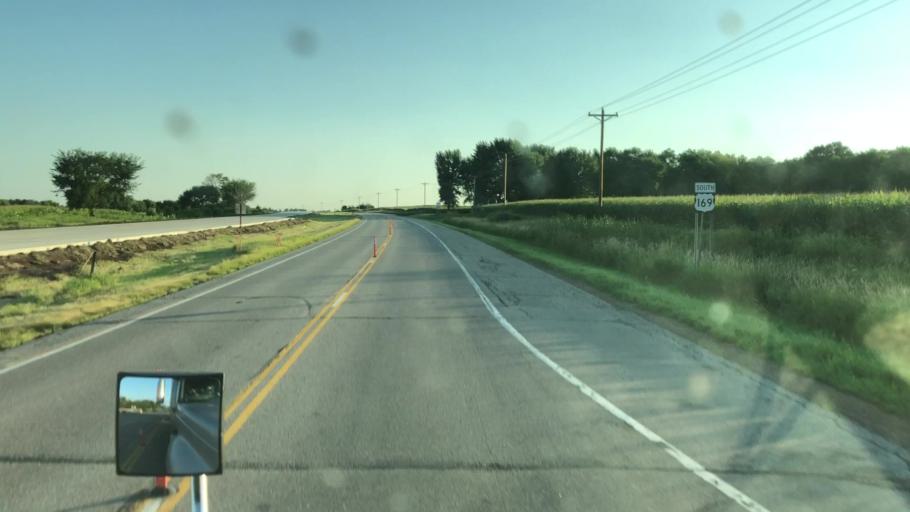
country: US
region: Minnesota
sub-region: Scott County
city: Belle Plaine
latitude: 44.5864
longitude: -93.8294
